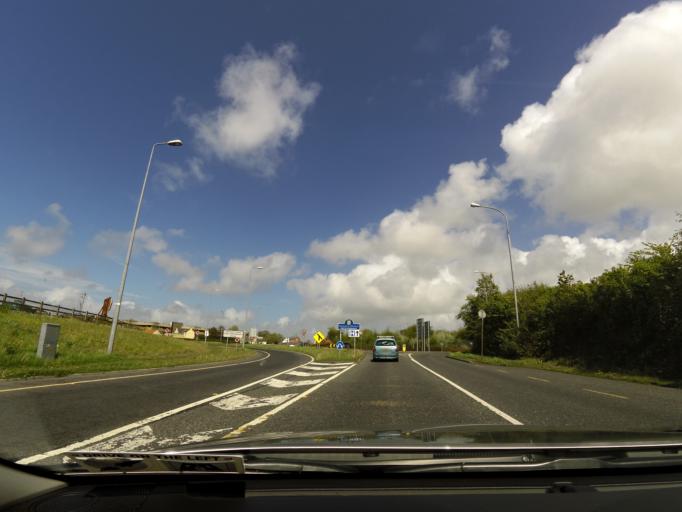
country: IE
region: Connaught
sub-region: County Galway
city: Oranmore
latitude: 53.2787
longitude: -8.9741
